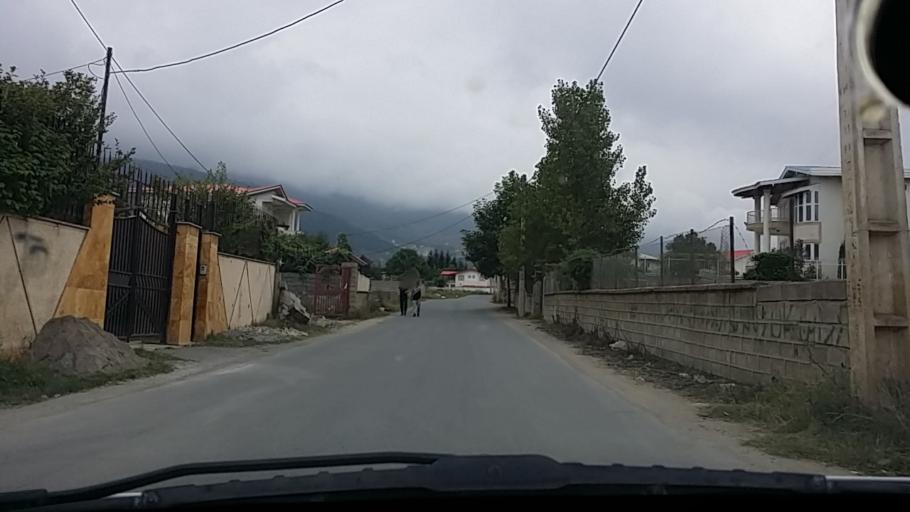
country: IR
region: Mazandaran
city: `Abbasabad
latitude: 36.5111
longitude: 51.1697
